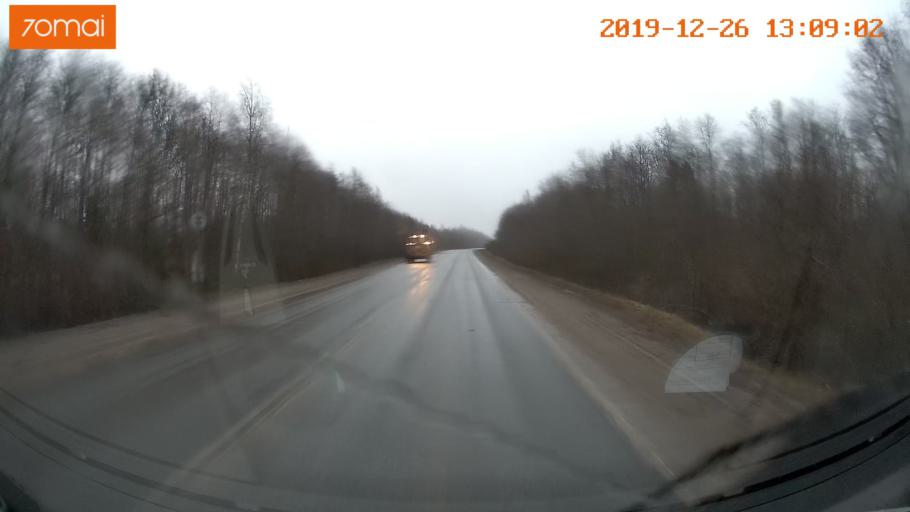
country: RU
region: Vologda
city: Cherepovets
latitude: 59.0514
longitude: 37.9486
